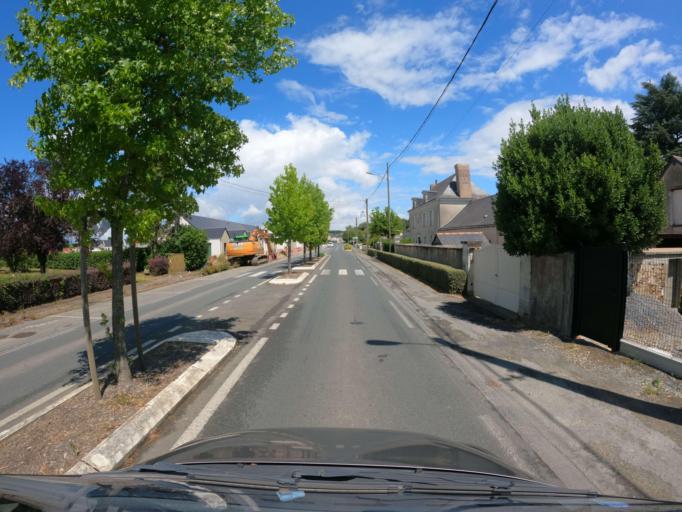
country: FR
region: Pays de la Loire
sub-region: Departement de Maine-et-Loire
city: Champigne
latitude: 47.6595
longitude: -0.5740
